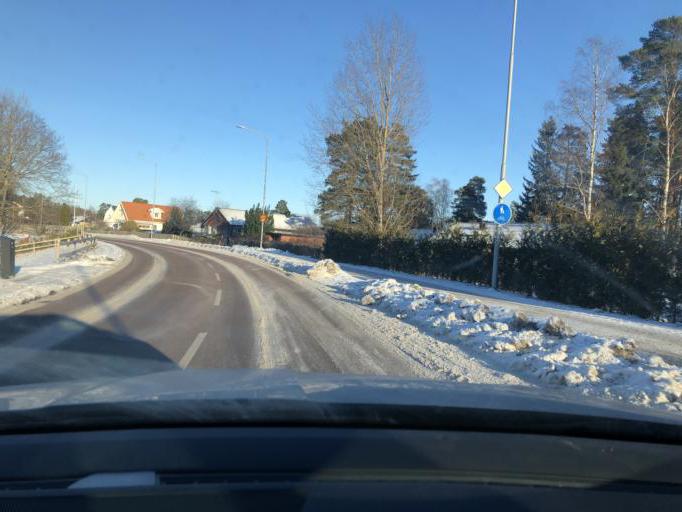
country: SE
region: Vaestmanland
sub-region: Vasteras
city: Hokasen
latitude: 59.6619
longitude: 16.5907
